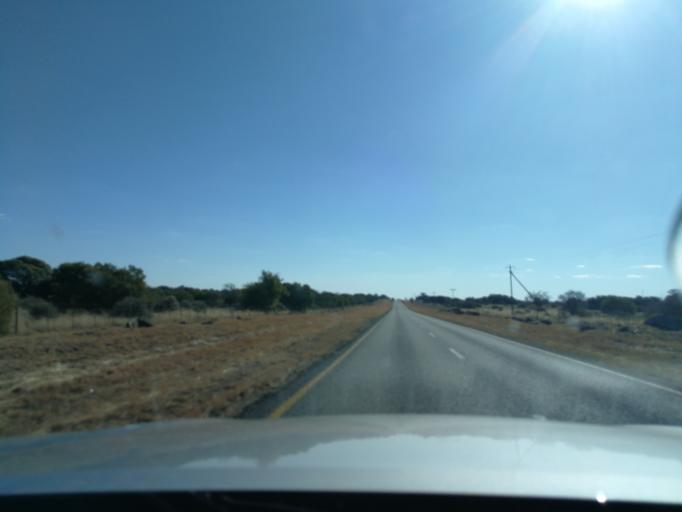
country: ZA
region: North-West
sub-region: Ngaka Modiri Molema District Municipality
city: Zeerust
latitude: -25.7660
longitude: 25.9820
